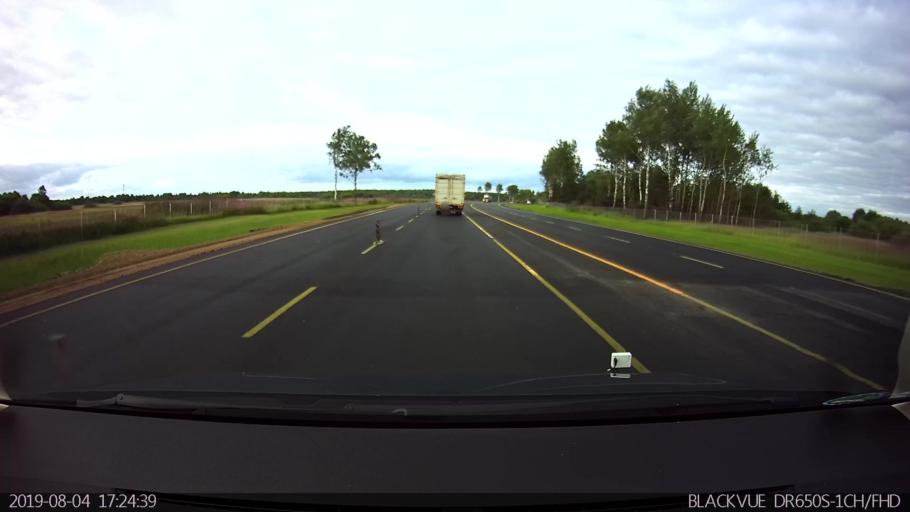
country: RU
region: Smolensk
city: Gagarin
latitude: 55.4859
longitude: 34.9457
